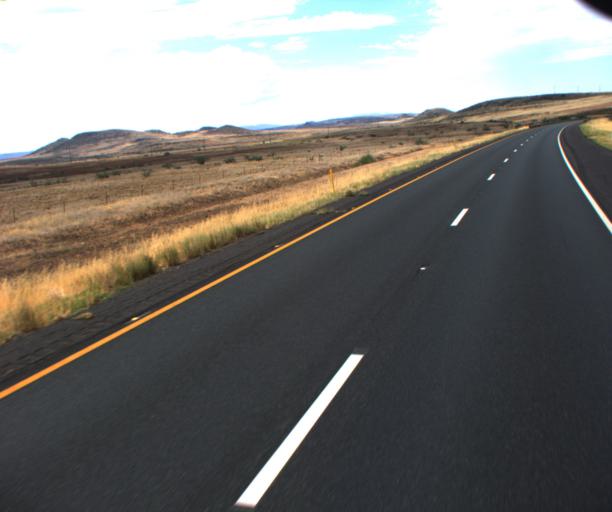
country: US
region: Arizona
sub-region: Yavapai County
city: Cordes Lakes
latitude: 34.4503
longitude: -112.0351
